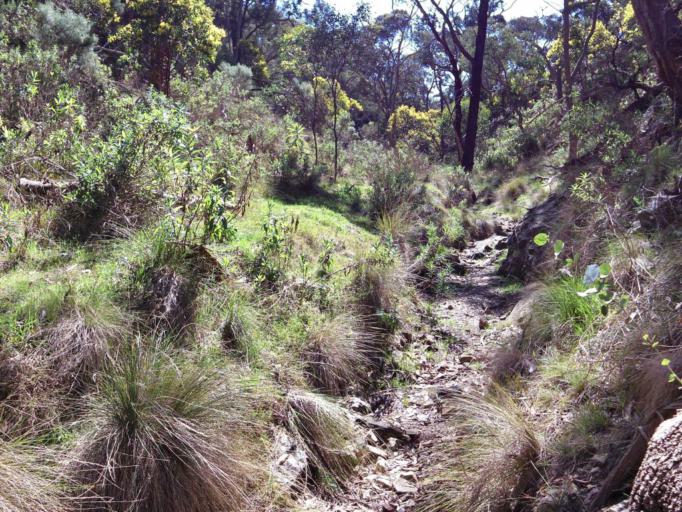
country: AU
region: Victoria
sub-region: Moorabool
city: Bacchus Marsh
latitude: -37.6646
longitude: 144.3146
